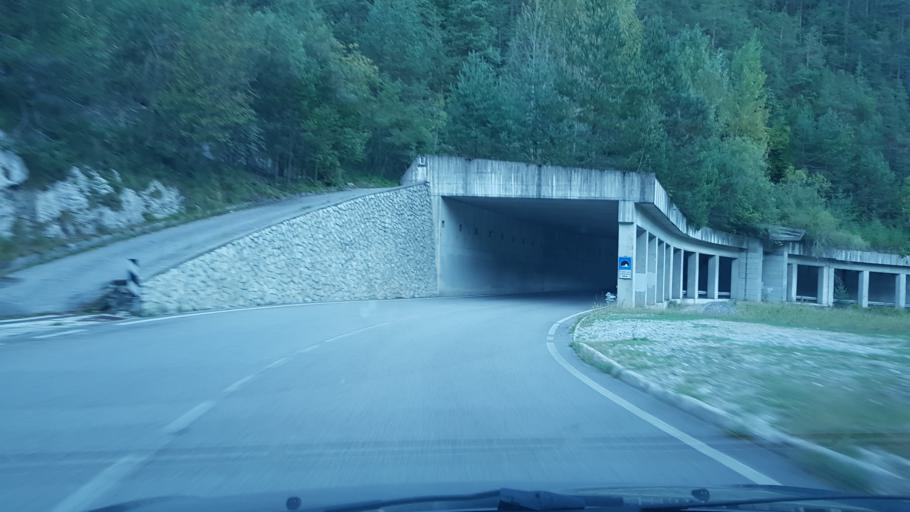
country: IT
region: Veneto
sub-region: Provincia di Belluno
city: Forno di Zoldo
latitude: 46.3327
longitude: 12.2315
